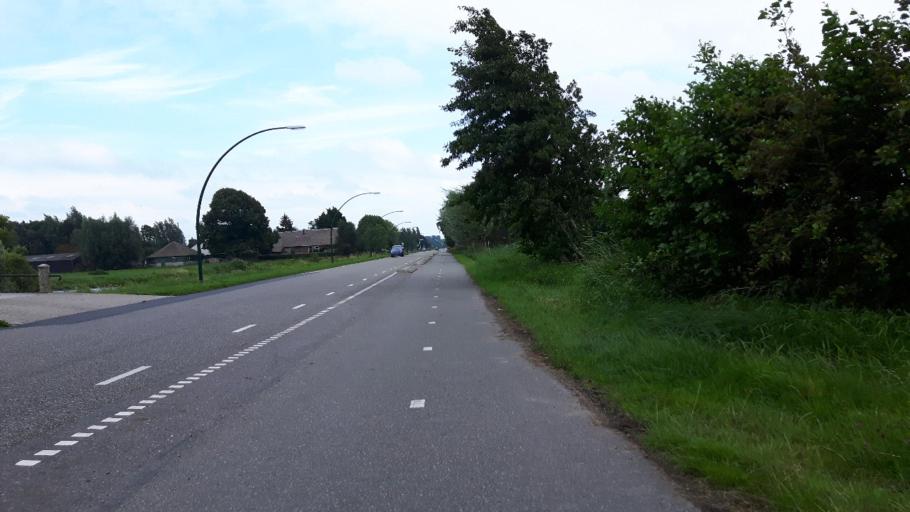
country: NL
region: Utrecht
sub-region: Gemeente Woerden
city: Woerden
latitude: 52.1074
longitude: 4.8473
